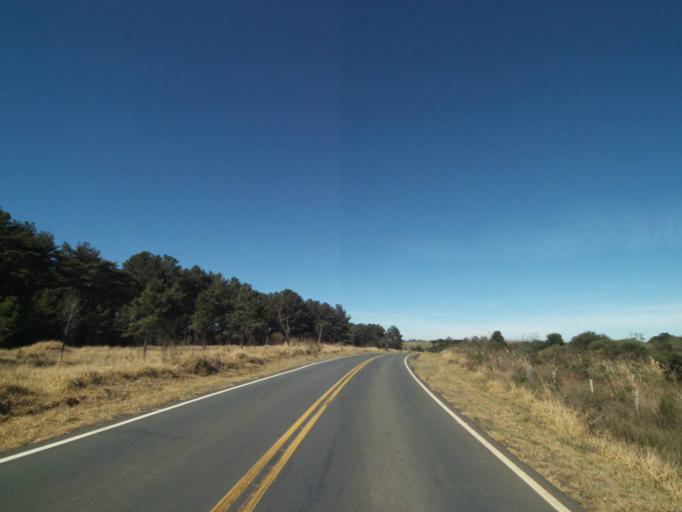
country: BR
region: Parana
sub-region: Castro
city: Castro
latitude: -24.7231
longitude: -50.1856
